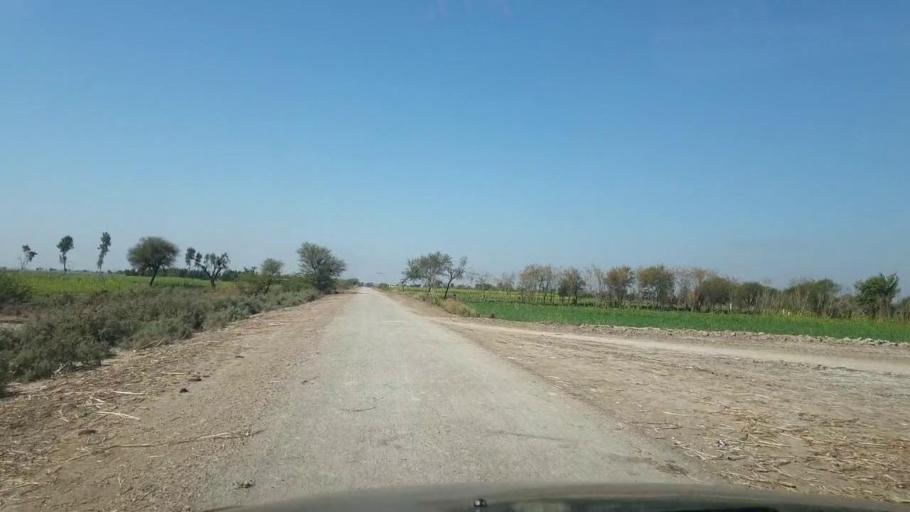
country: PK
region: Sindh
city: Mirpur Khas
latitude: 25.5865
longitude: 69.0748
